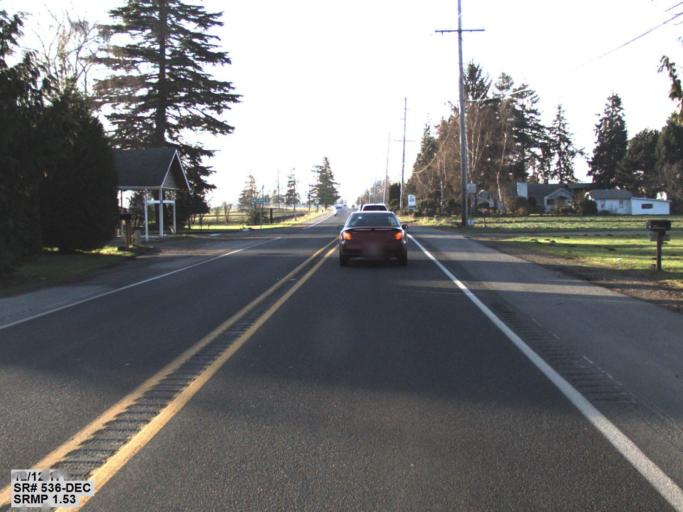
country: US
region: Washington
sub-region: Skagit County
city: Mount Vernon
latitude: 48.4428
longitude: -122.3999
